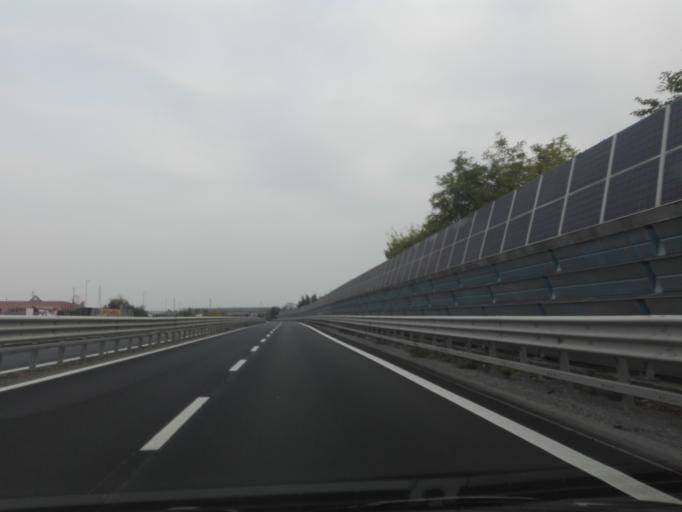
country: IT
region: Veneto
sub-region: Provincia di Verona
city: Vallese
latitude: 45.3313
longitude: 11.0790
